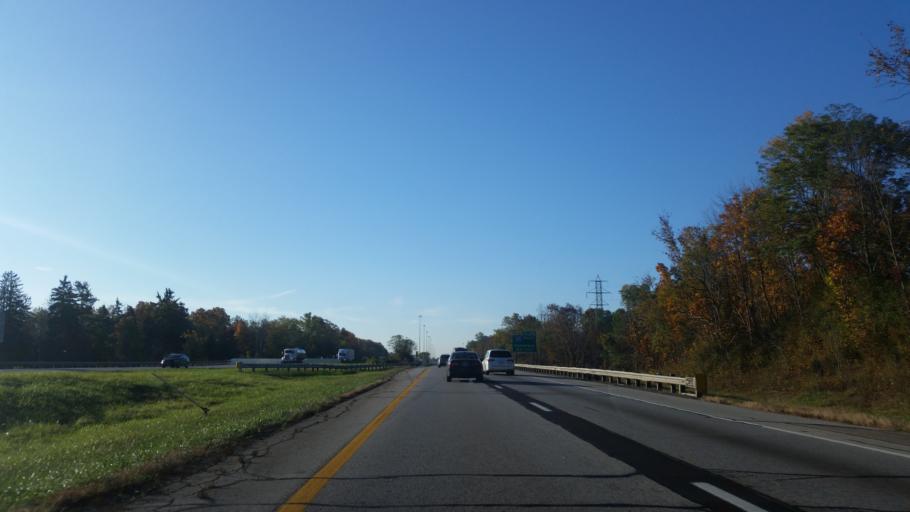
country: US
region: Ohio
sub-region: Summit County
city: Richfield
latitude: 41.2414
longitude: -81.6288
